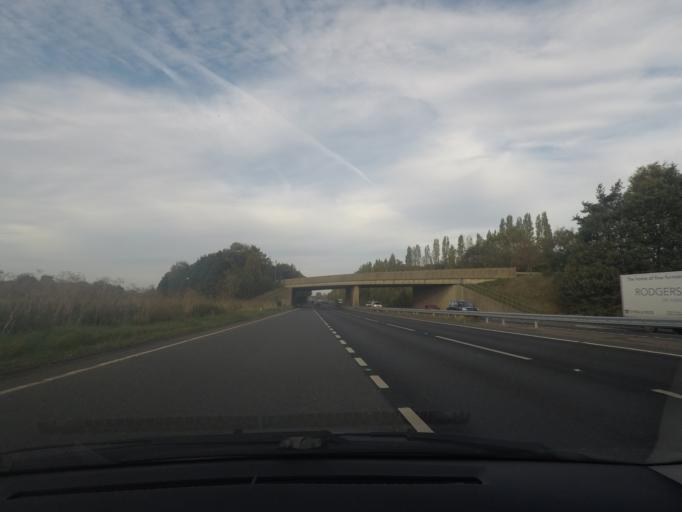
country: GB
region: England
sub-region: City of York
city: Fulford
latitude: 53.9261
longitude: -1.0739
